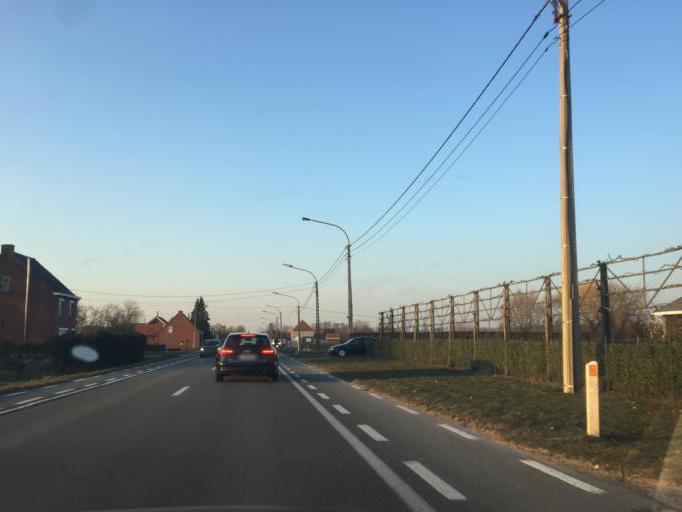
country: BE
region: Flanders
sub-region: Provincie West-Vlaanderen
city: Pittem
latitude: 50.9743
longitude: 3.2420
